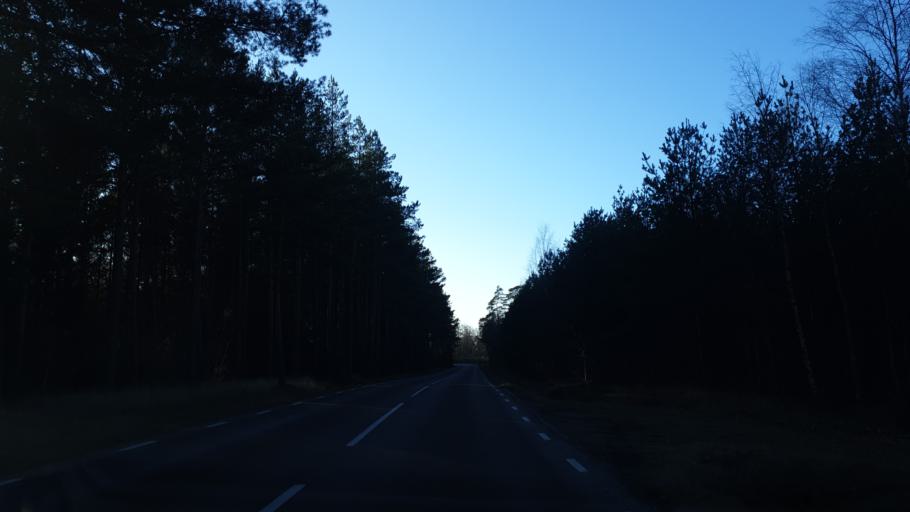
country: SE
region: Blekinge
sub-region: Ronneby Kommun
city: Kallinge
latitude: 56.2089
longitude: 15.3854
